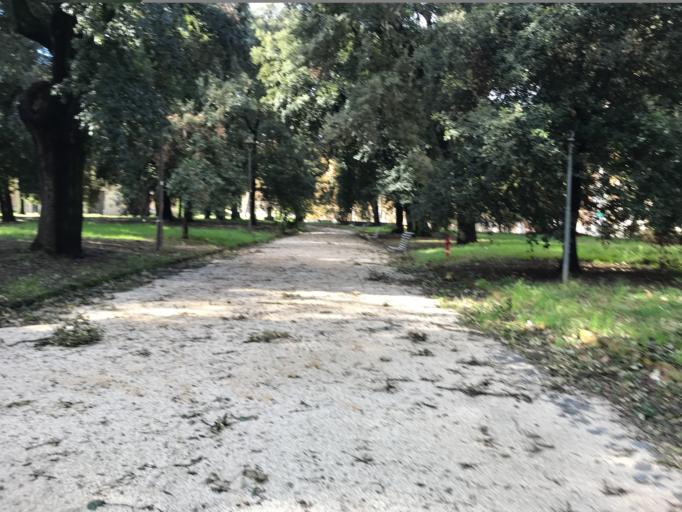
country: IT
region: Latium
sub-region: Citta metropolitana di Roma Capitale
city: Rome
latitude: 41.9149
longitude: 12.5106
